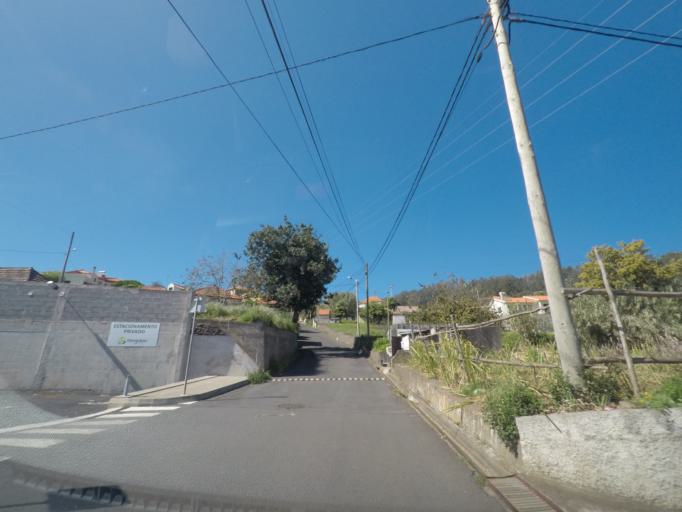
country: PT
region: Madeira
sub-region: Calheta
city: Arco da Calheta
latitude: 32.7077
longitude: -17.1165
